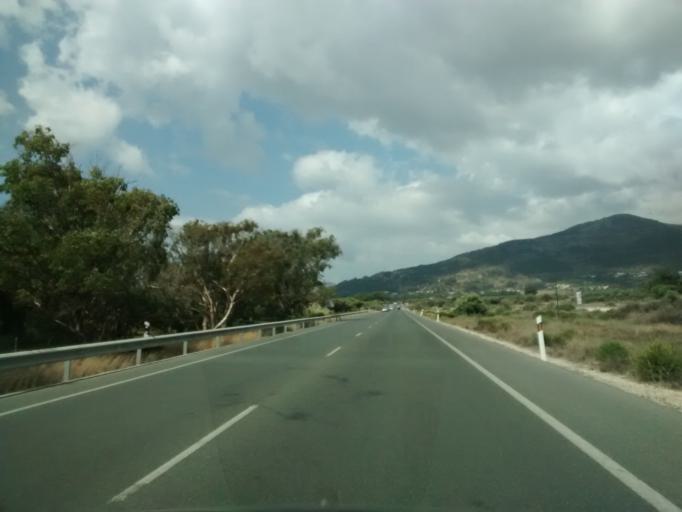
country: ES
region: Andalusia
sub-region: Provincia de Cadiz
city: Tarifa
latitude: 36.0466
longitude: -5.6365
